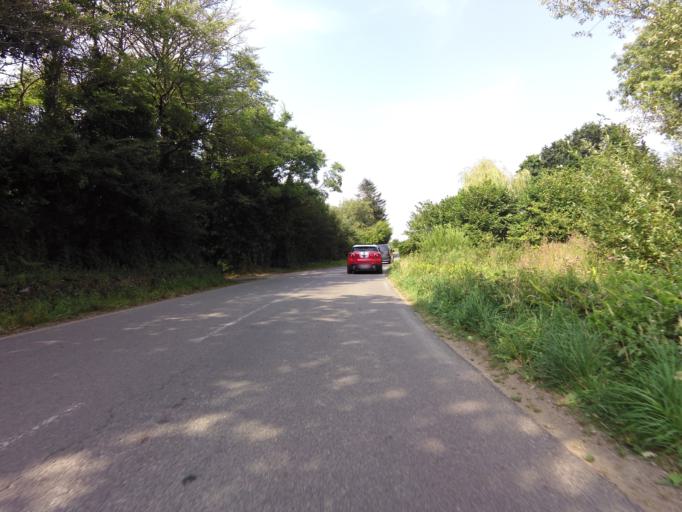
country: FR
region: Brittany
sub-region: Departement du Finistere
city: Esquibien
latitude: 48.0138
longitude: -4.5653
